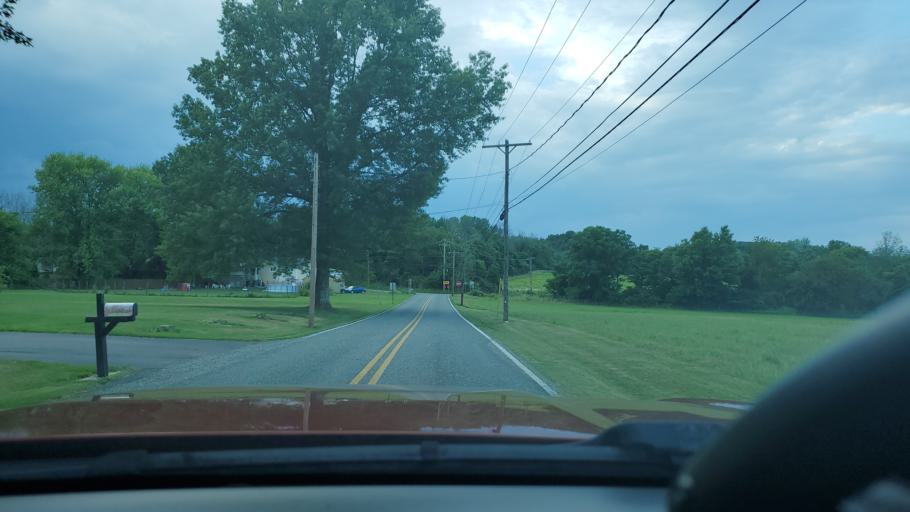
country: US
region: Pennsylvania
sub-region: Montgomery County
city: Limerick
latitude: 40.2502
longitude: -75.5212
